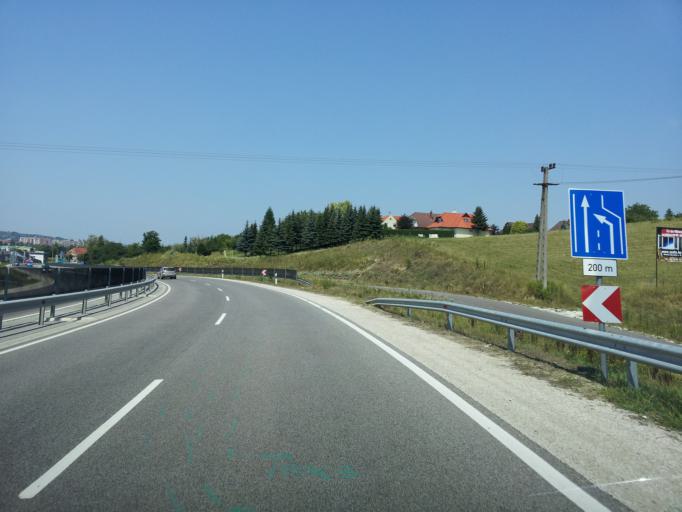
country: HU
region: Zala
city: Zalaegerszeg
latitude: 46.8403
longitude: 16.8844
